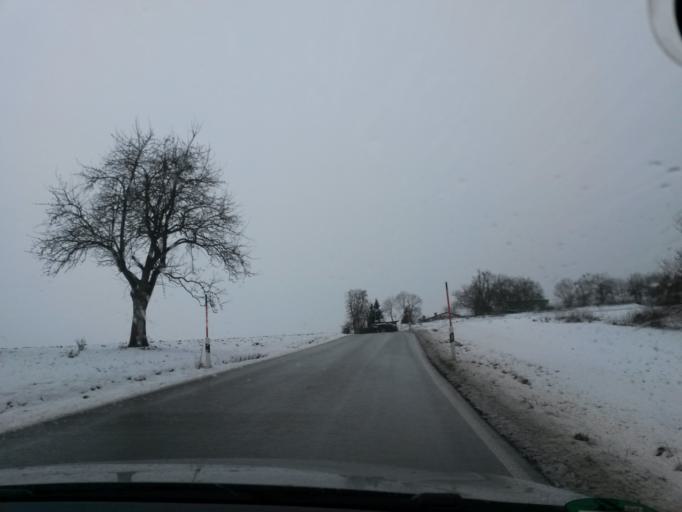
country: DE
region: Baden-Wuerttemberg
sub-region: Regierungsbezirk Stuttgart
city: Bad Uberkingen
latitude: 48.5840
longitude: 9.7936
